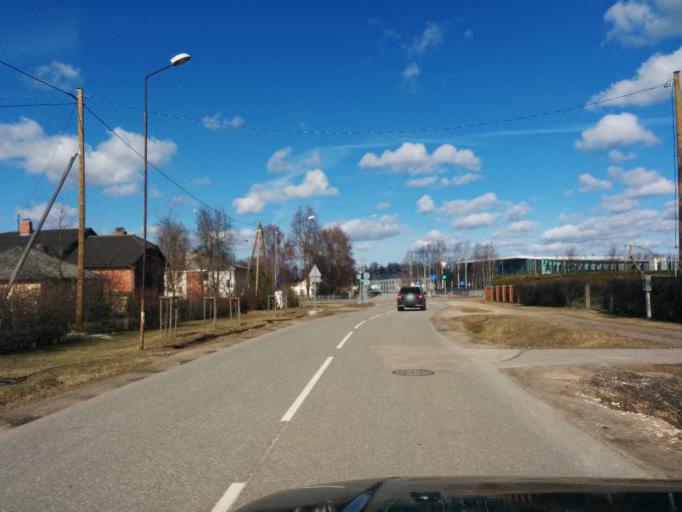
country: LV
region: Jelgava
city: Jelgava
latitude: 56.6583
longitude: 23.7549
